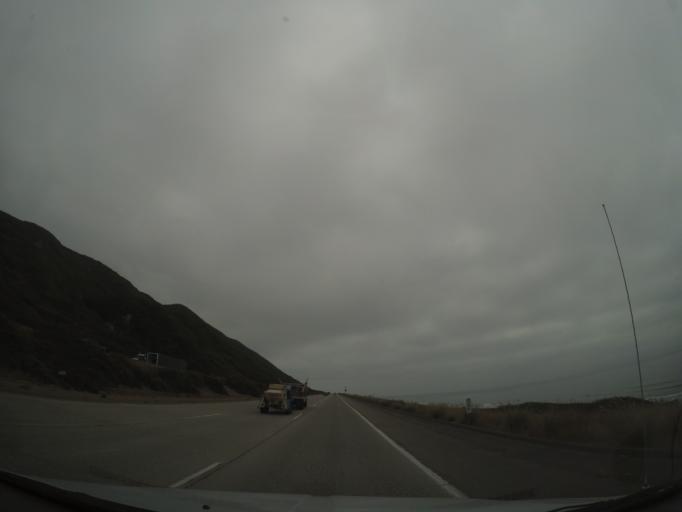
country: US
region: California
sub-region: Ventura County
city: Ventura
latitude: 34.3304
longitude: -119.3988
